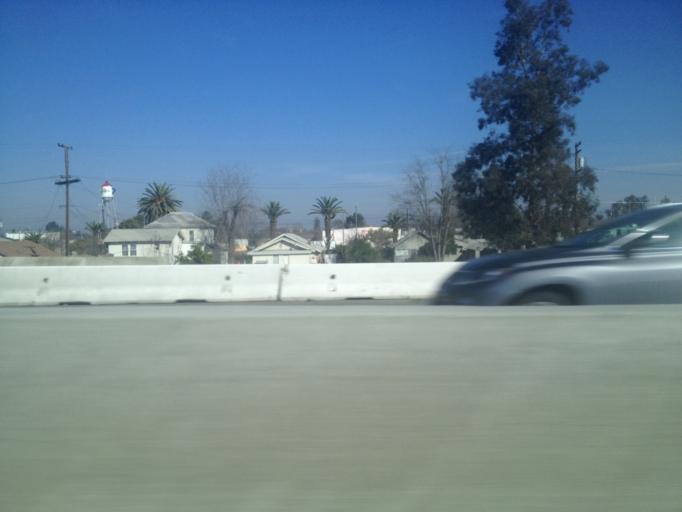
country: US
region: California
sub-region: Fresno County
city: Kingsburg
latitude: 36.5114
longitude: -119.5538
